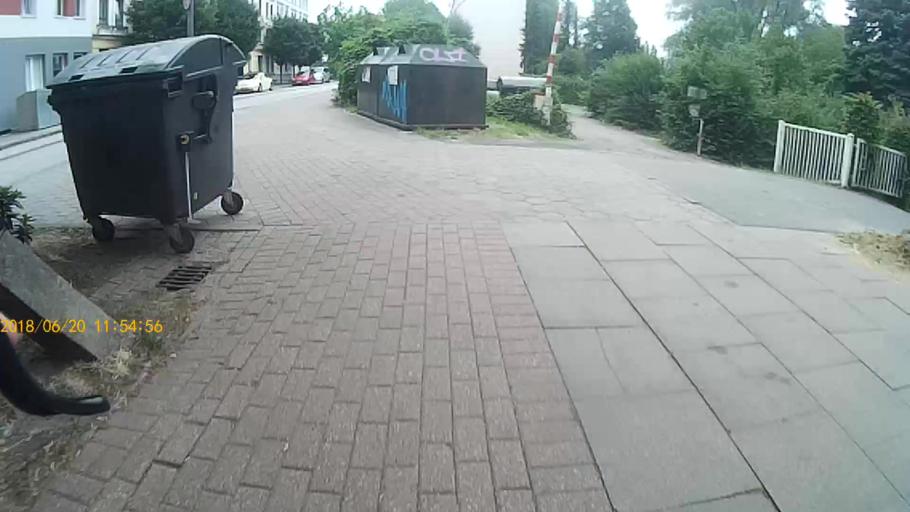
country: DE
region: Hamburg
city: Rothenburgsort
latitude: 53.5141
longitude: 10.0206
